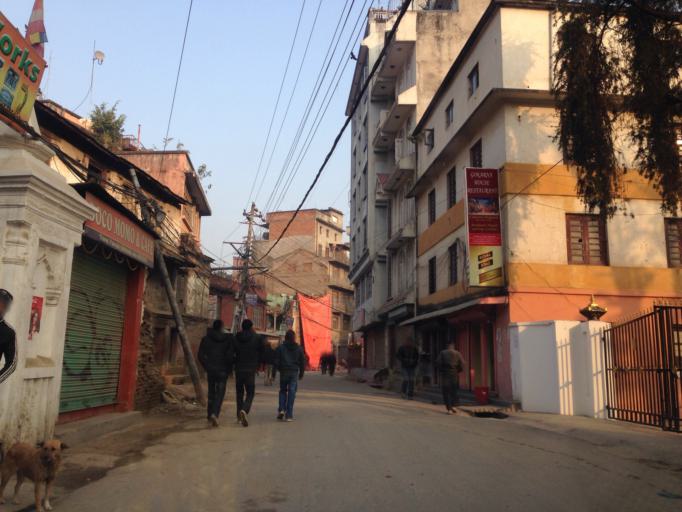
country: NP
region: Central Region
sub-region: Bagmati Zone
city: Kathmandu
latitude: 27.7135
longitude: 85.3086
